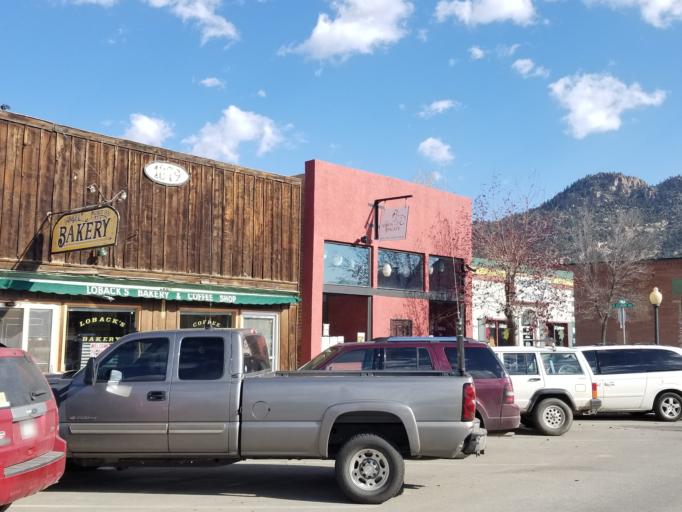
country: US
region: Colorado
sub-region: Chaffee County
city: Buena Vista
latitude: 38.8427
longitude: -106.1297
